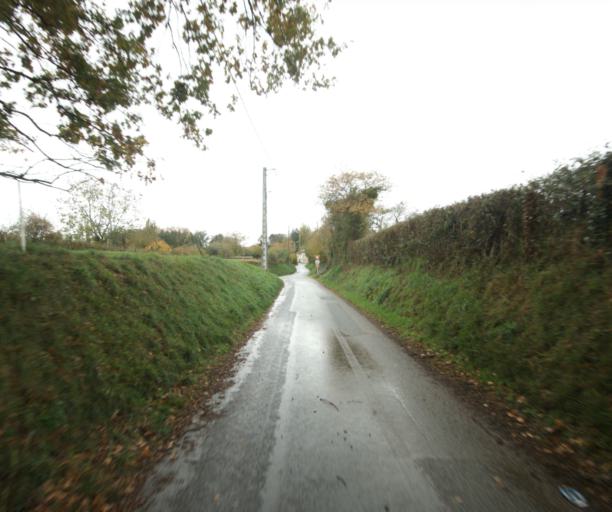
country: FR
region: Rhone-Alpes
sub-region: Departement de l'Ain
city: Pont-de-Vaux
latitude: 46.4839
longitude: 4.8690
